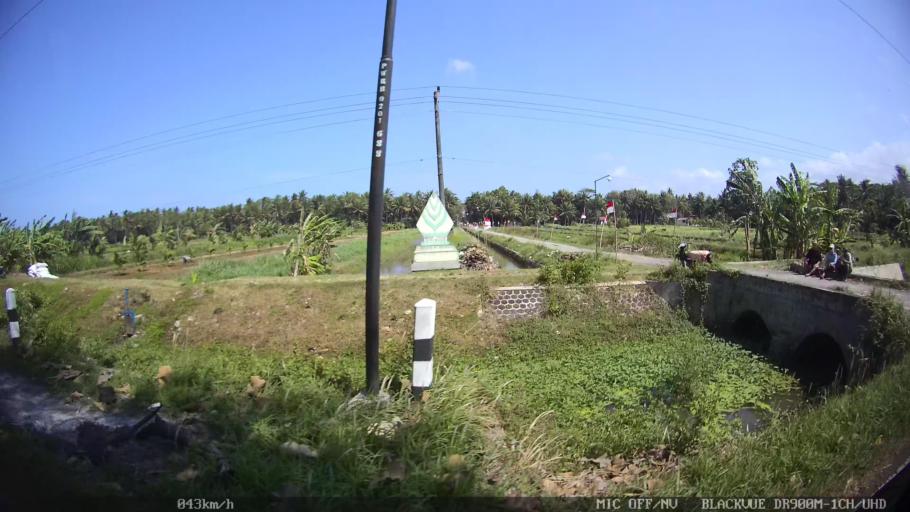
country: ID
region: Daerah Istimewa Yogyakarta
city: Srandakan
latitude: -7.9281
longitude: 110.1561
